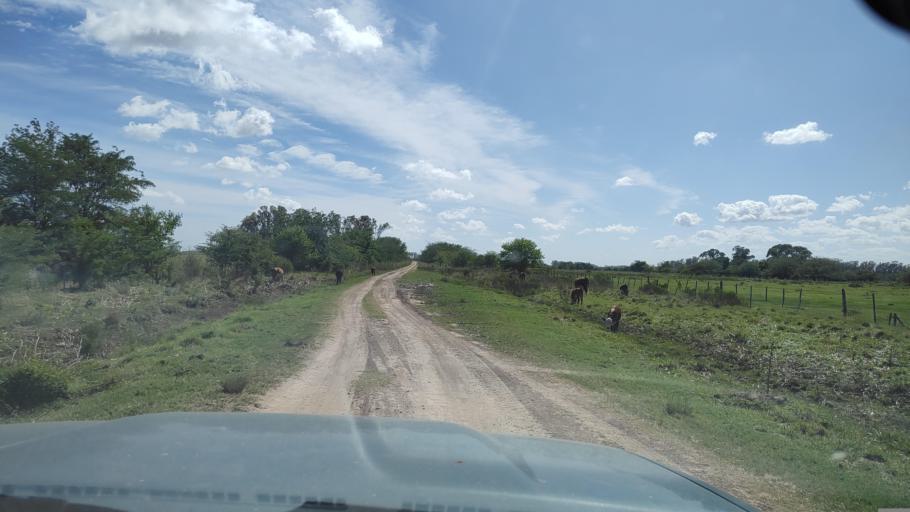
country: AR
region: Buenos Aires
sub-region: Partido de Lujan
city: Lujan
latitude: -34.5212
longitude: -59.1687
